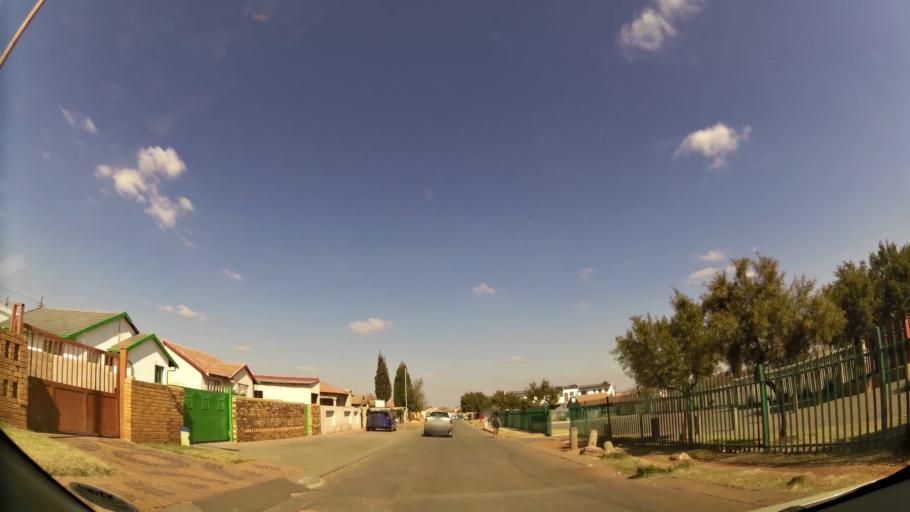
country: ZA
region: Gauteng
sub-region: West Rand District Municipality
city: Krugersdorp
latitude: -26.1496
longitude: 27.7719
